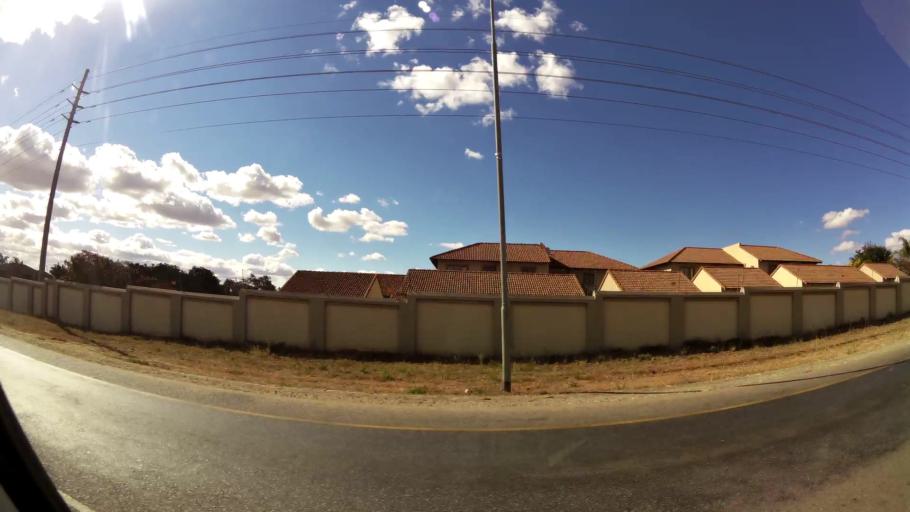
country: ZA
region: Limpopo
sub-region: Capricorn District Municipality
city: Polokwane
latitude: -23.8806
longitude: 29.4972
